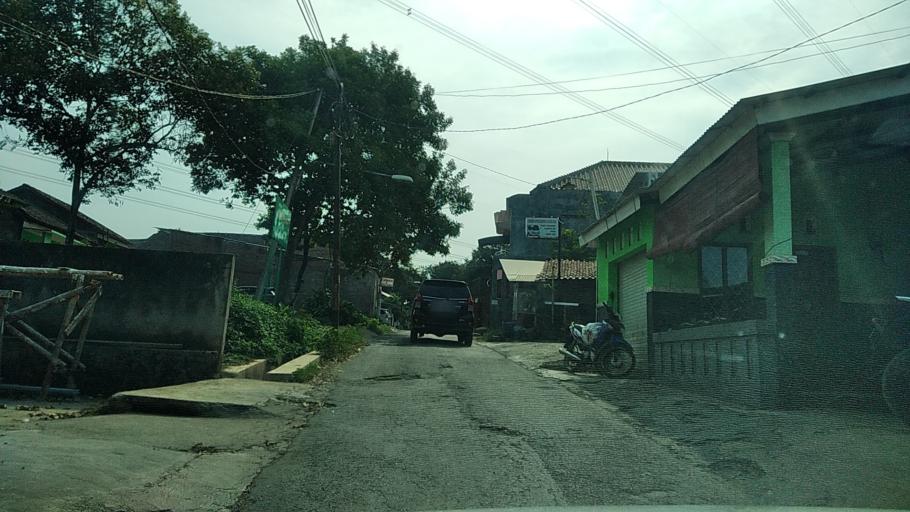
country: ID
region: Central Java
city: Ungaran
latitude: -7.0567
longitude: 110.3085
